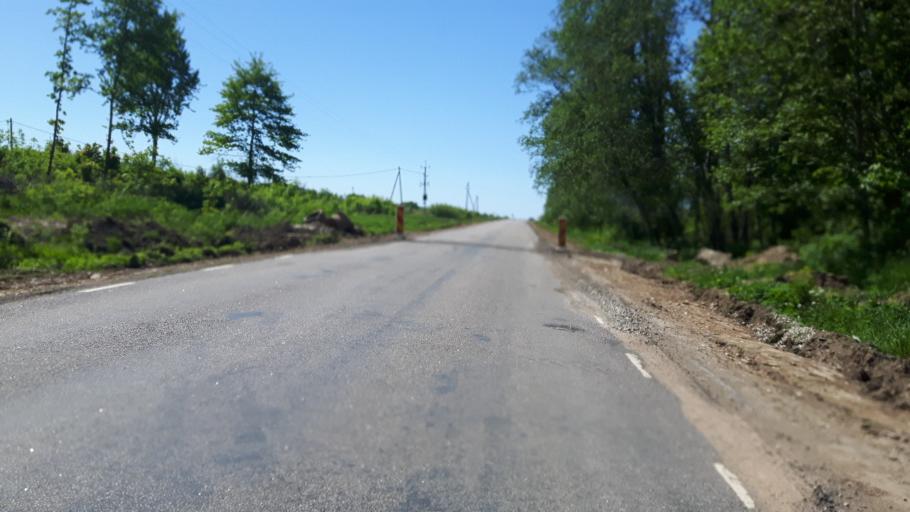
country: EE
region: Ida-Virumaa
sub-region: Narva-Joesuu linn
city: Narva-Joesuu
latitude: 59.4044
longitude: 27.9392
